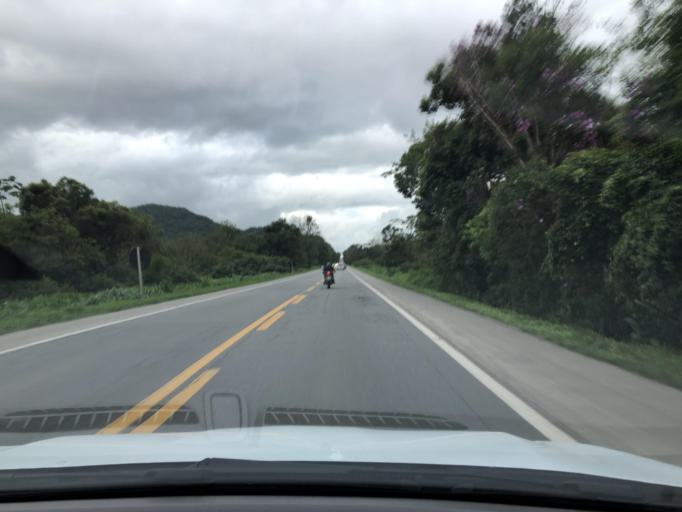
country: BR
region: Santa Catarina
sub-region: Sao Francisco Do Sul
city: Sao Francisco do Sul
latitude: -26.3253
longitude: -48.6494
